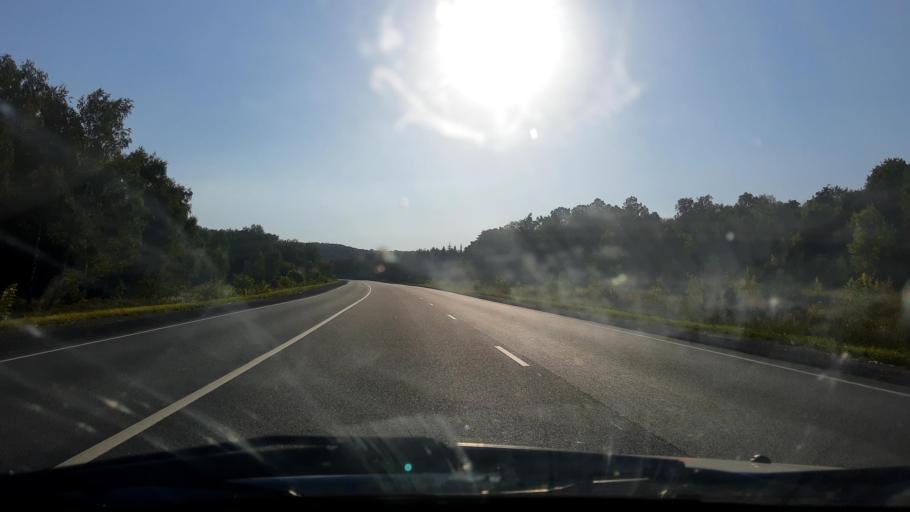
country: RU
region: Bashkortostan
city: Oktyabr'skiy
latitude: 54.4320
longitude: 53.4792
